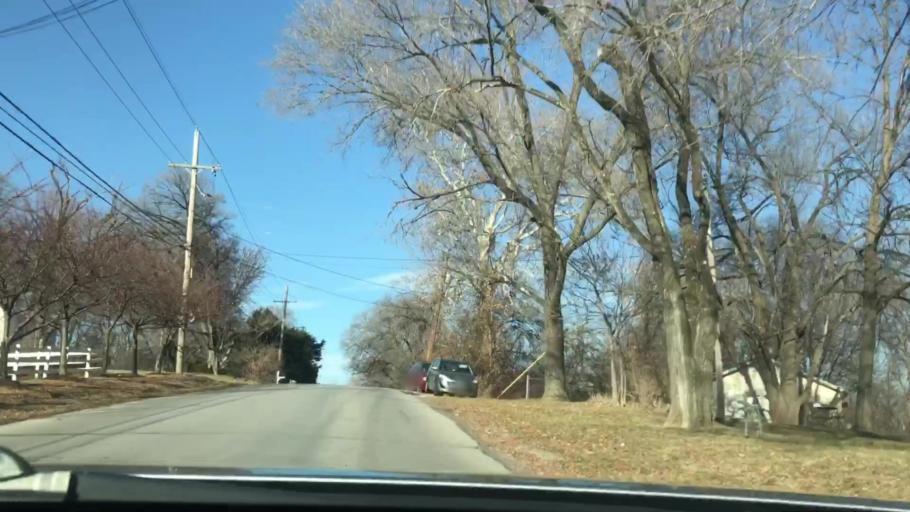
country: US
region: Missouri
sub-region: Platte County
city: Parkville
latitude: 39.2052
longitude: -94.6871
